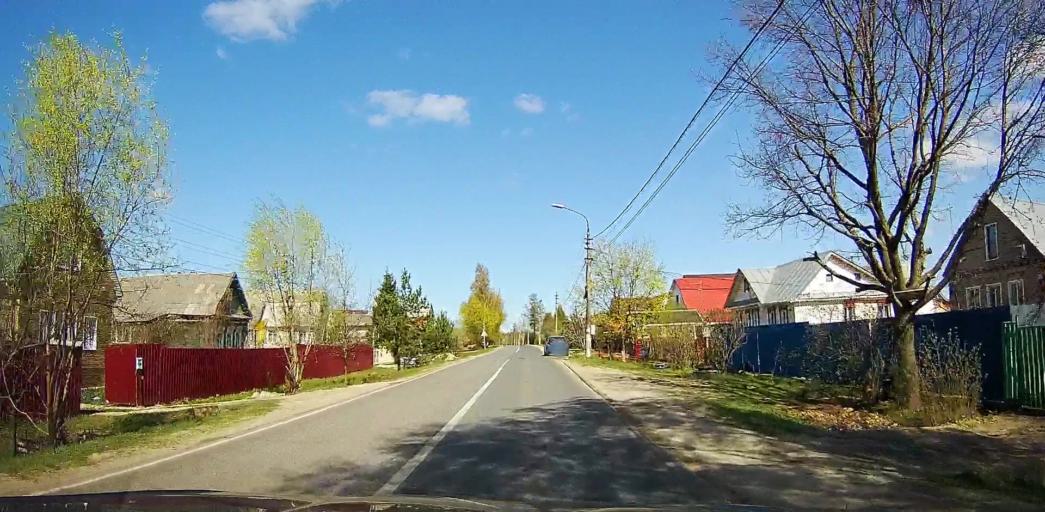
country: RU
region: Moskovskaya
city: Ramenskoye
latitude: 55.6173
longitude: 38.3032
